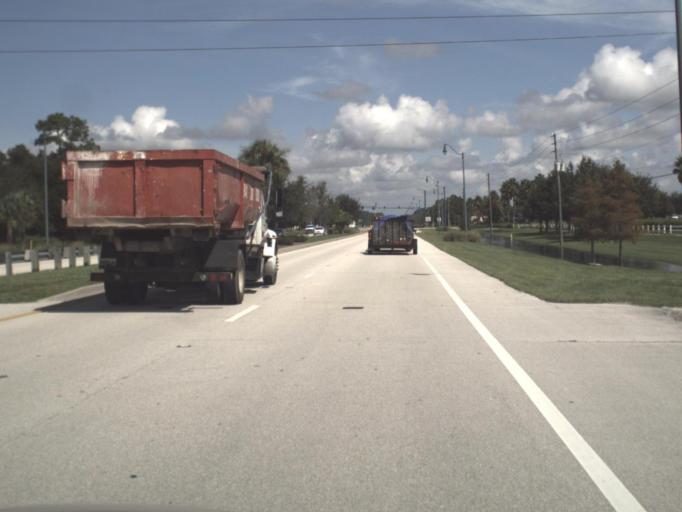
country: US
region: Florida
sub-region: Sarasota County
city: North Port
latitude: 27.0760
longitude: -82.1555
